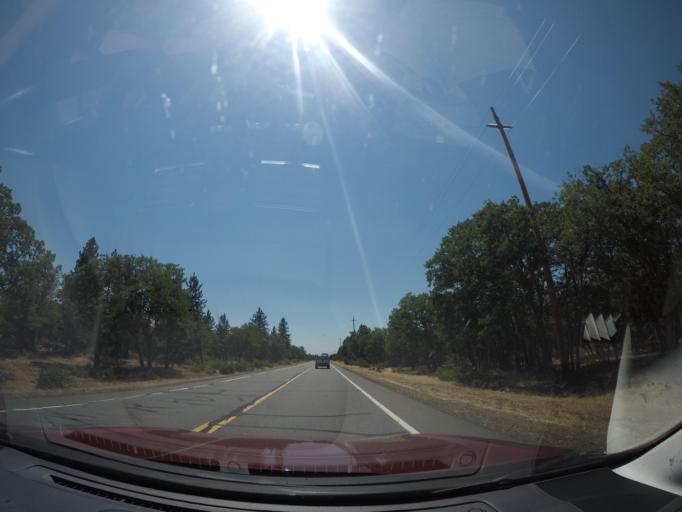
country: US
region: California
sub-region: Shasta County
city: Burney
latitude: 41.0929
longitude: -121.3063
